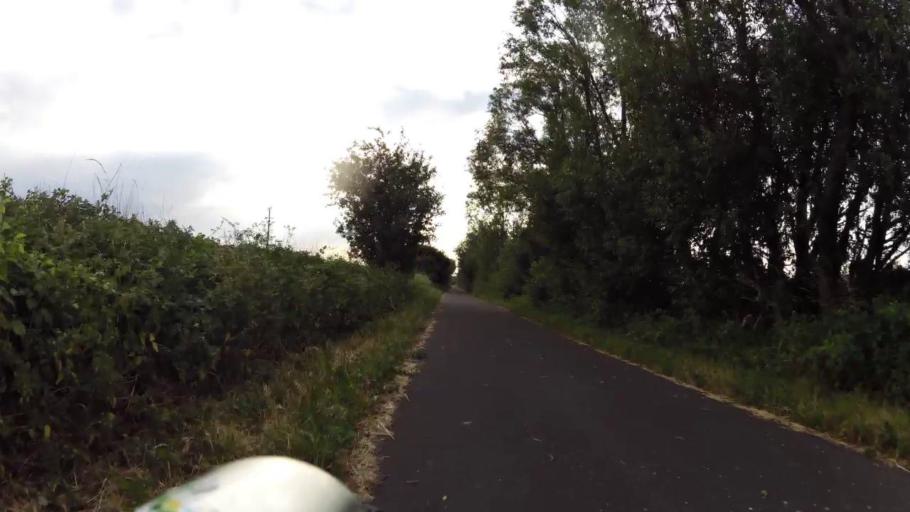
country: PL
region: Kujawsko-Pomorskie
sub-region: Powiat chelminski
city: Unislaw
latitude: 53.1808
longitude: 18.4032
